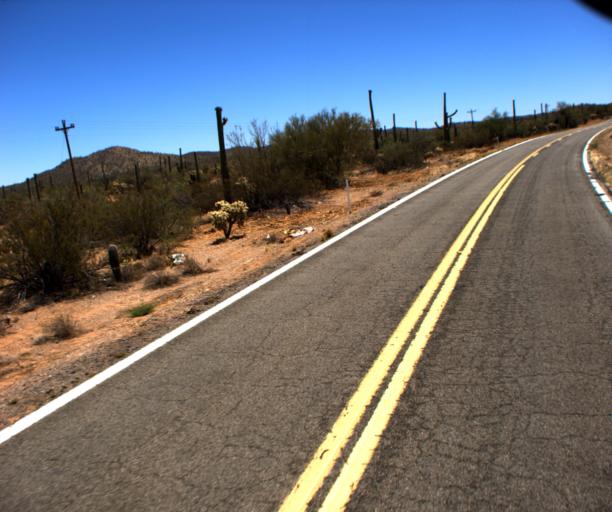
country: US
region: Arizona
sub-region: Pima County
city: Sells
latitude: 32.1764
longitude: -112.2362
